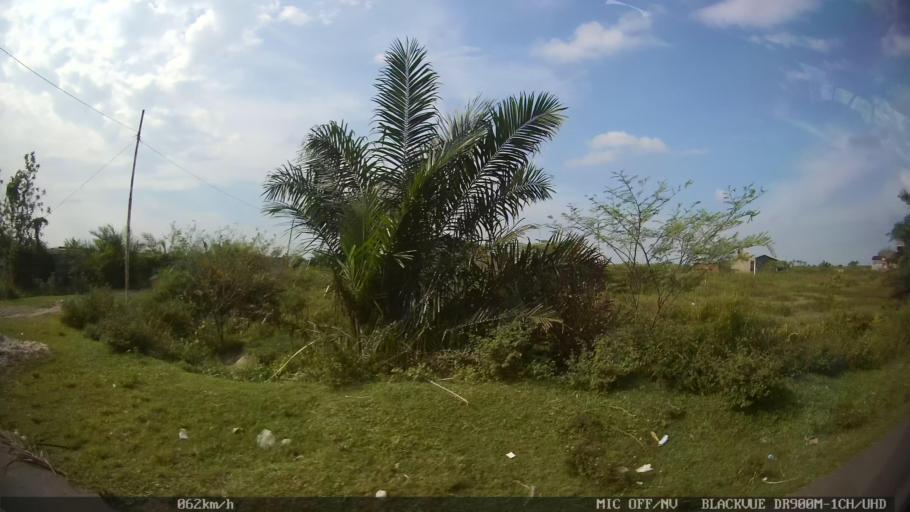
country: ID
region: North Sumatra
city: Medan
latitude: 3.5731
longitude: 98.7629
